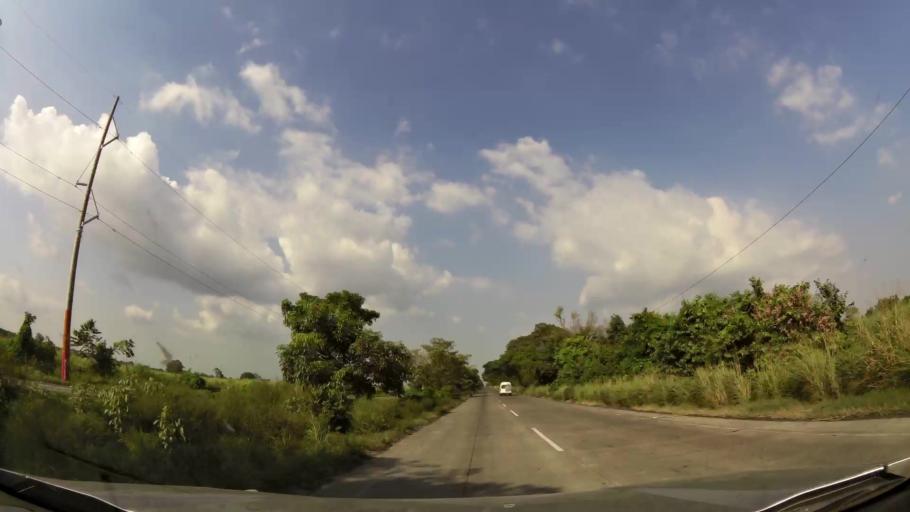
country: GT
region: Escuintla
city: Puerto San Jose
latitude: 14.0154
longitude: -90.7841
